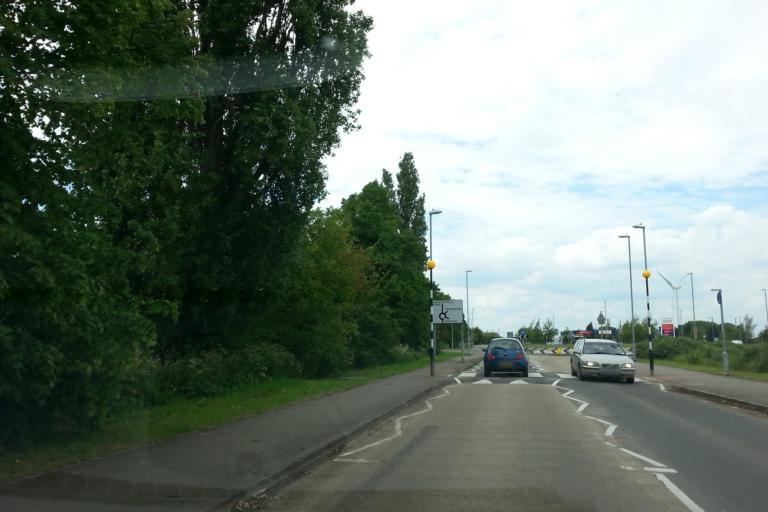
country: GB
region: England
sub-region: Cambridgeshire
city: Ramsey
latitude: 52.4546
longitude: -0.1129
